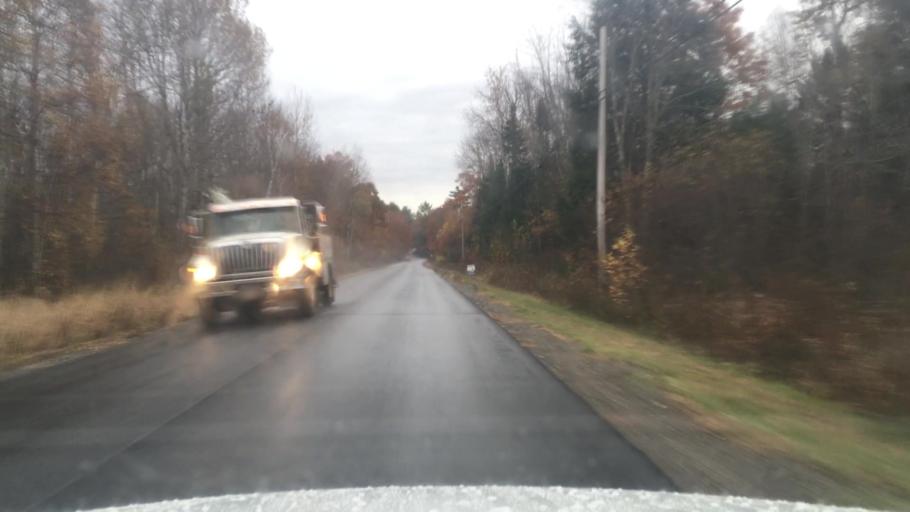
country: US
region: Maine
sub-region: Waldo County
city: Lincolnville
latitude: 44.3157
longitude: -69.0742
